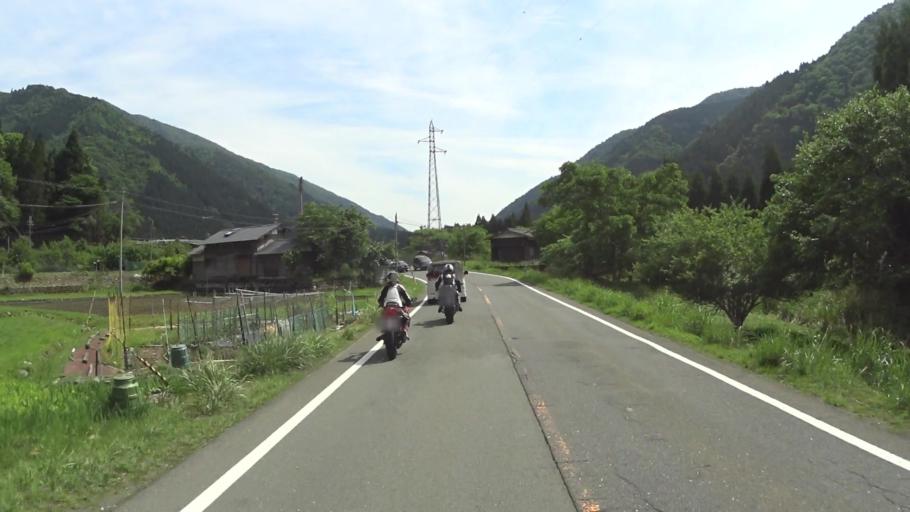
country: JP
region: Shiga Prefecture
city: Kitahama
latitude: 35.2910
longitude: 135.8835
